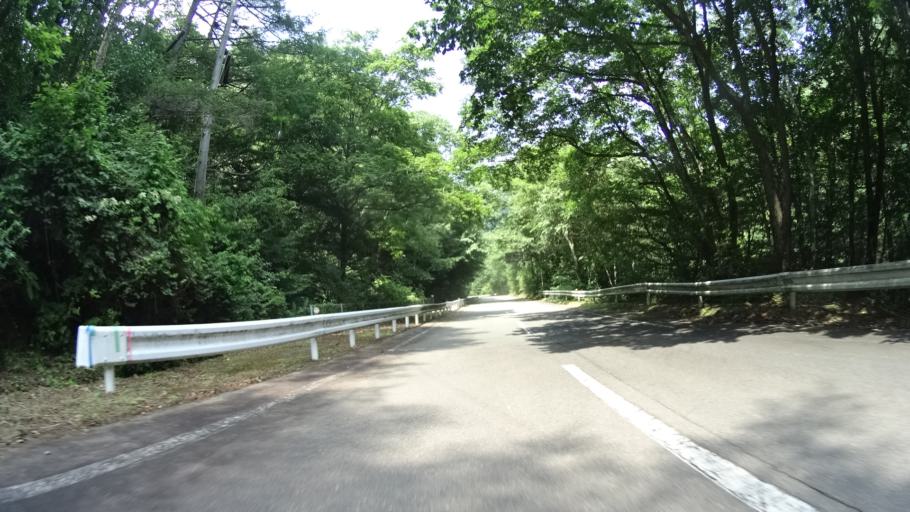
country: JP
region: Nagano
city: Saku
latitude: 36.1199
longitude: 138.6095
